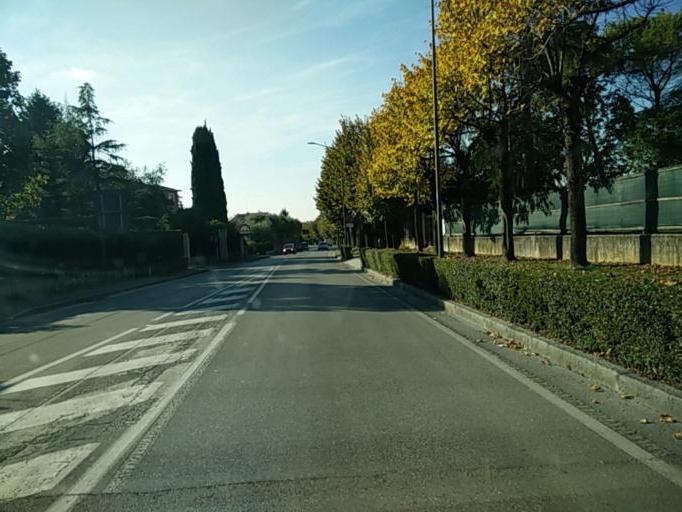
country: IT
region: Lombardy
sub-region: Provincia di Brescia
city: Desenzano del Garda
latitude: 45.4610
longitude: 10.5650
